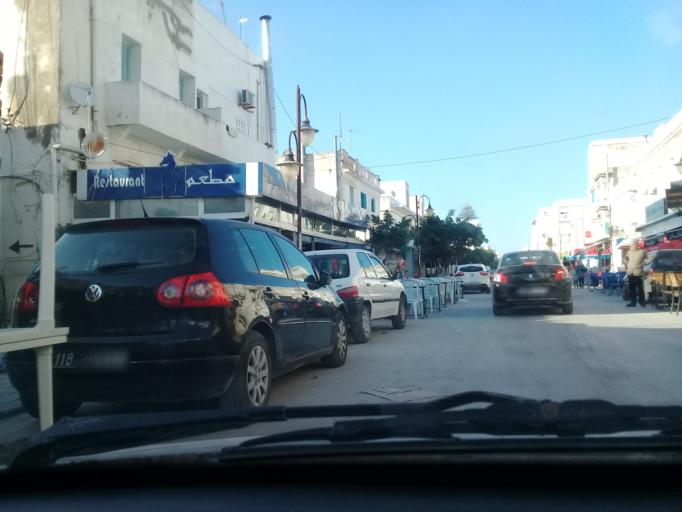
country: TN
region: Tunis
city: La Goulette
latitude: 36.8188
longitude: 10.3073
